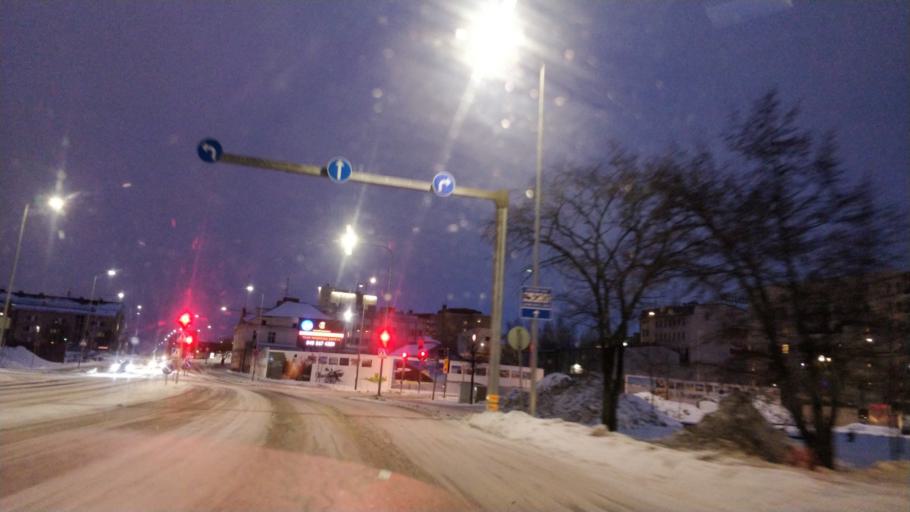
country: FI
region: Lapland
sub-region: Kemi-Tornio
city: Kemi
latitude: 65.7390
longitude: 24.5658
